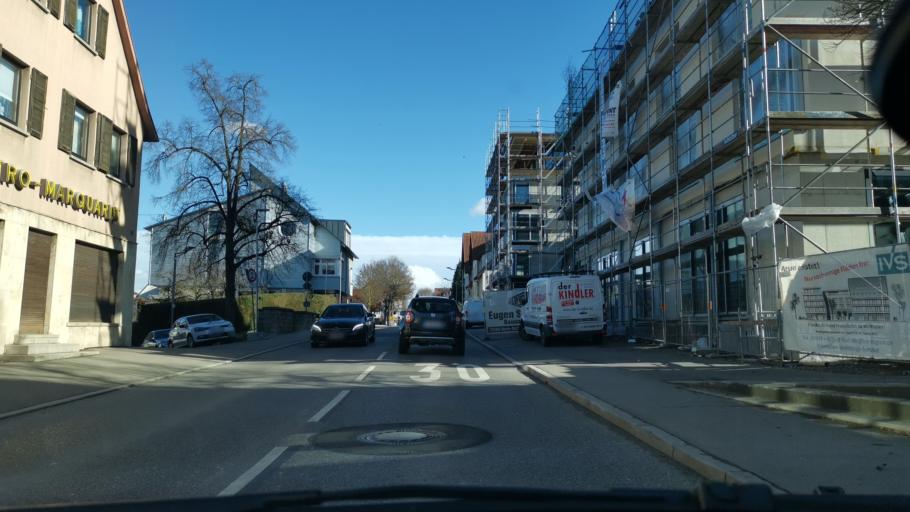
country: DE
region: Baden-Wuerttemberg
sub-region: Regierungsbezirk Stuttgart
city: Ehningen
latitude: 48.6911
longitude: 8.9499
